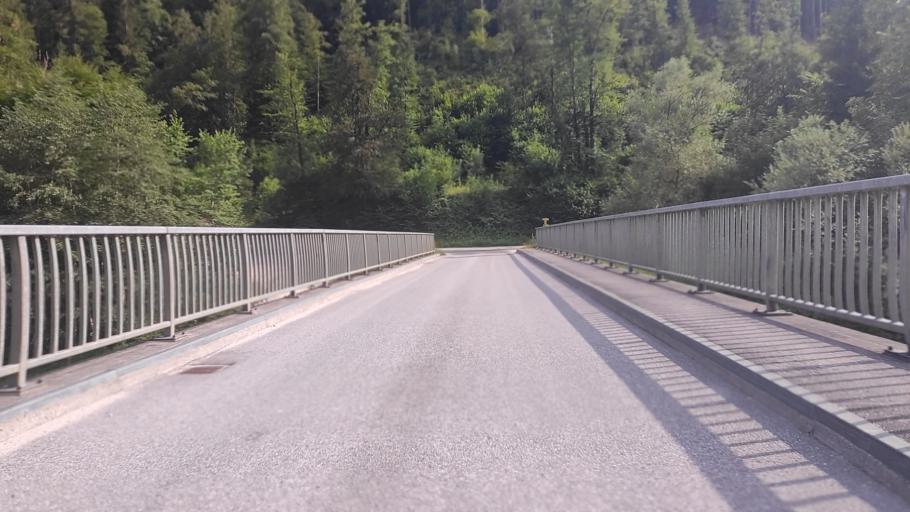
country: AT
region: Salzburg
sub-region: Politischer Bezirk Zell am See
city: Unken
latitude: 47.6633
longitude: 12.7562
